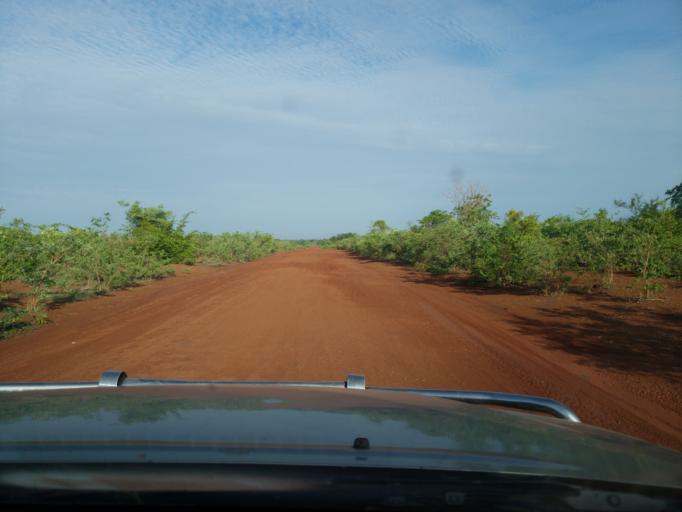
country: ML
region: Sikasso
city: Koutiala
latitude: 12.4262
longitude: -5.6432
